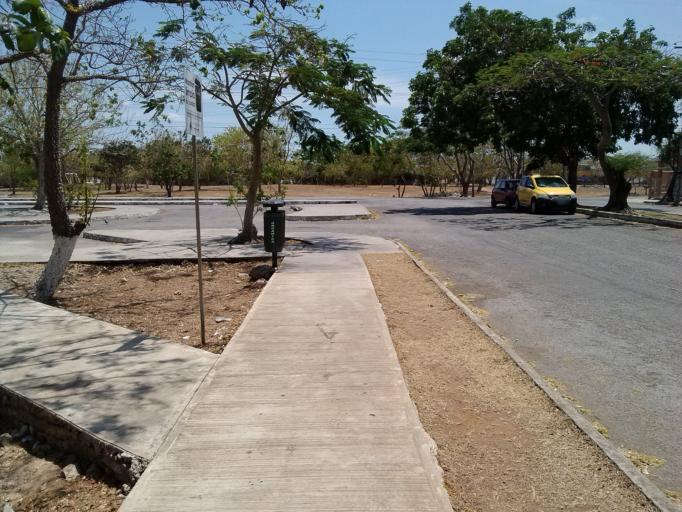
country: MX
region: Yucatan
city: Merida
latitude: 20.9677
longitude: -89.5833
